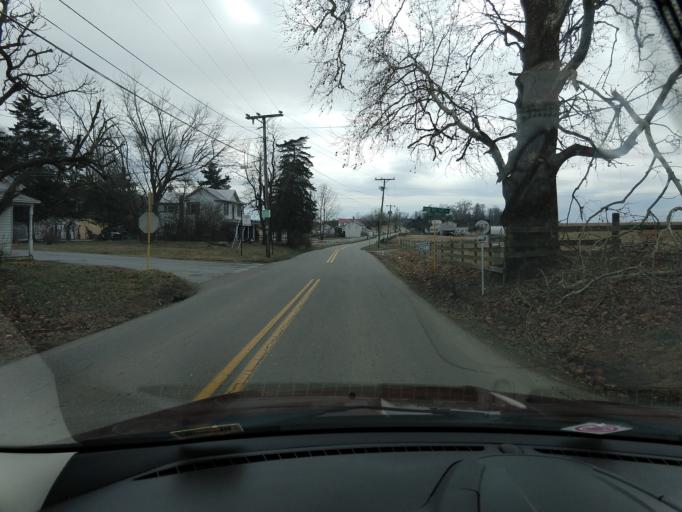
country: US
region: Virginia
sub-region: Augusta County
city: Crimora
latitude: 38.1957
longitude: -78.9080
